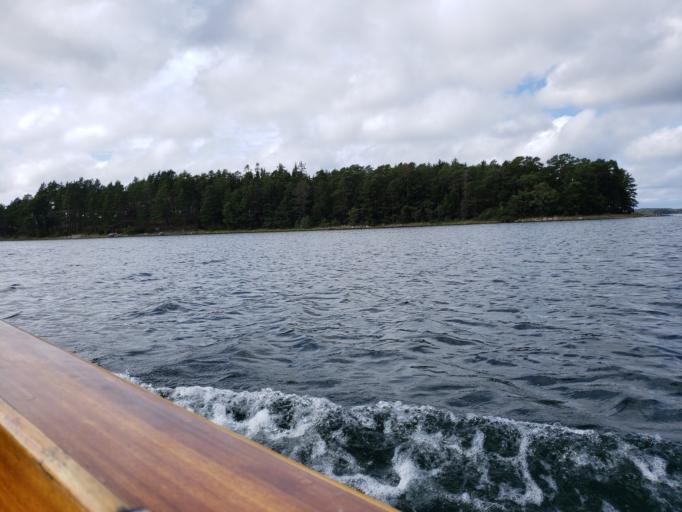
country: FI
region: Varsinais-Suomi
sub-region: Aboland-Turunmaa
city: Dragsfjaerd
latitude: 59.9167
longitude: 22.3966
